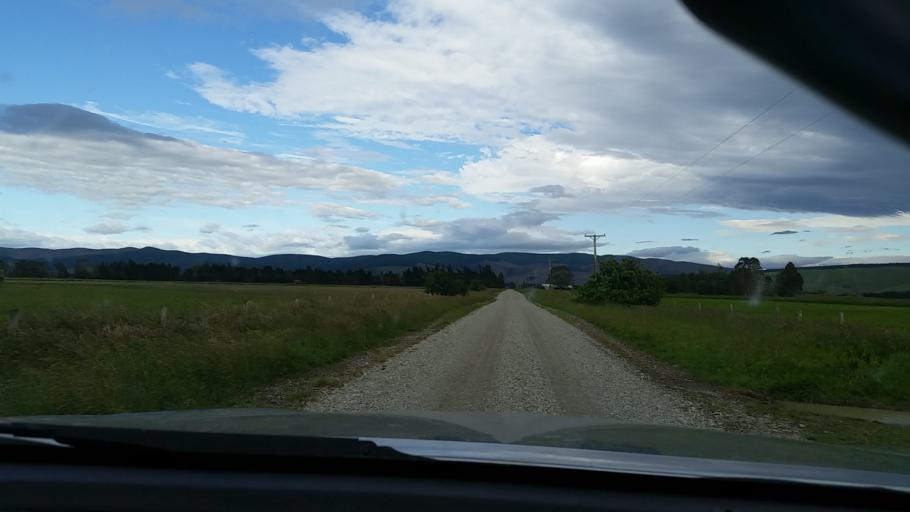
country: NZ
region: Southland
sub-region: Southland District
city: Winton
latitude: -45.8638
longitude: 168.3508
